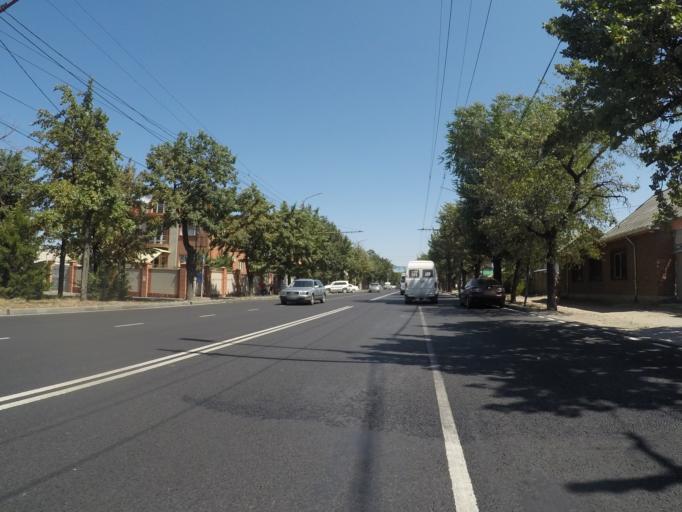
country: KG
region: Chuy
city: Bishkek
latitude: 42.8436
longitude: 74.5789
